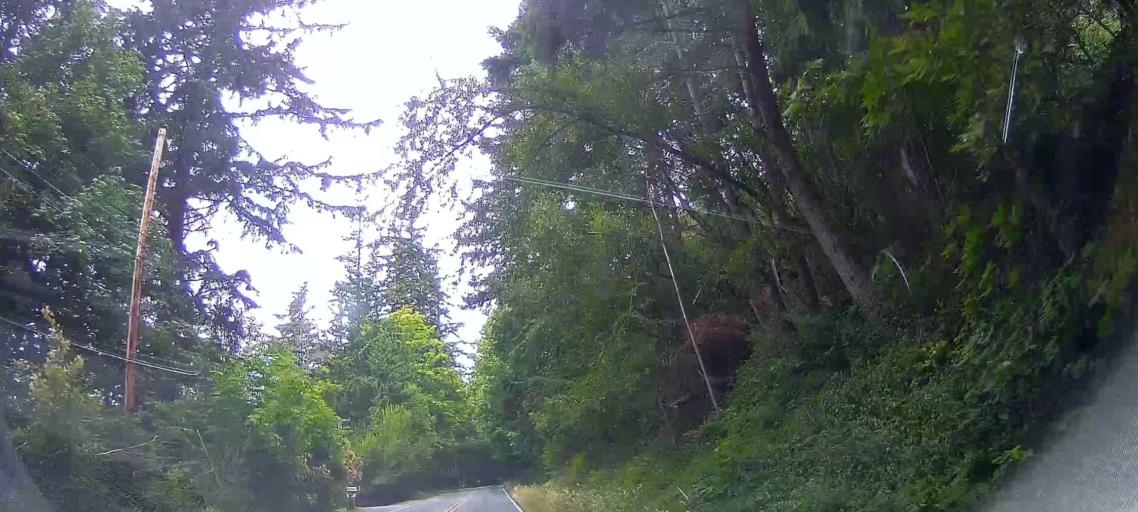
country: US
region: Washington
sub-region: Skagit County
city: Anacortes
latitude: 48.4535
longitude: -122.6338
